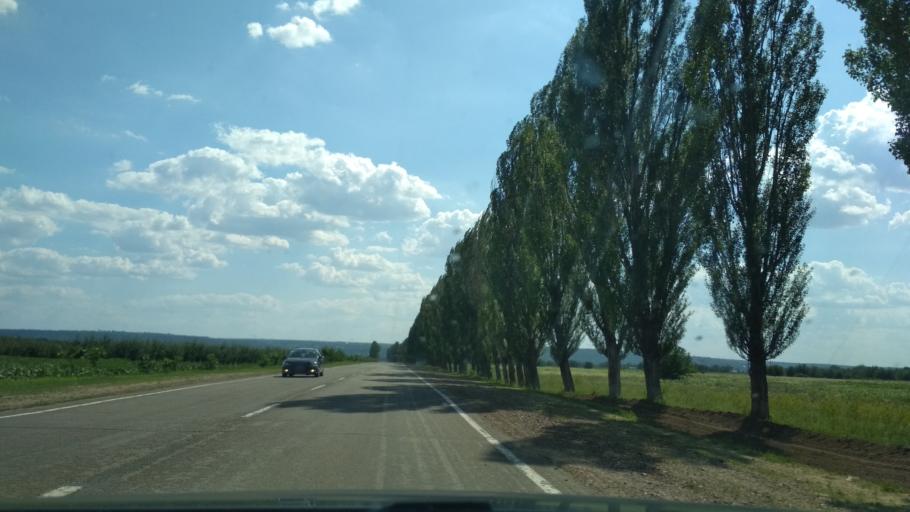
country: MD
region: Chisinau
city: Vadul lui Voda
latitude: 47.1298
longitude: 29.1243
